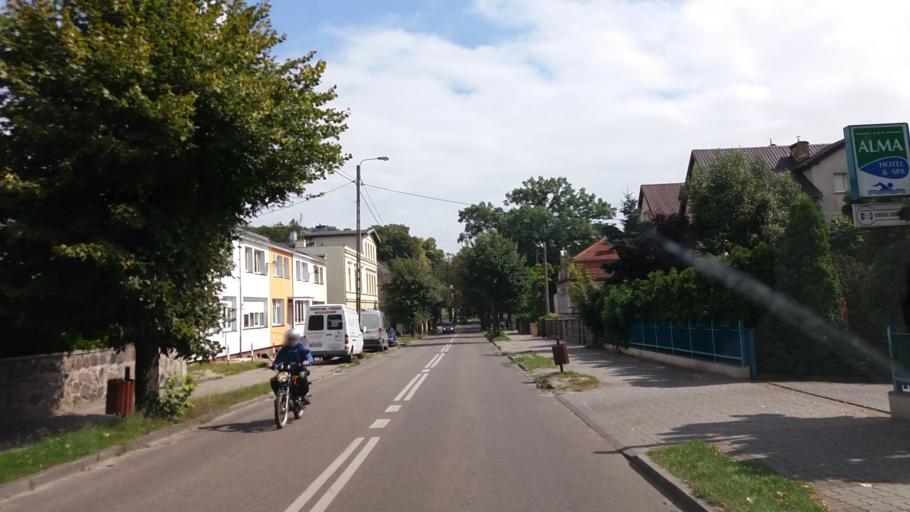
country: PL
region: West Pomeranian Voivodeship
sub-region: Powiat mysliborski
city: Barlinek
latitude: 52.9936
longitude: 15.2215
